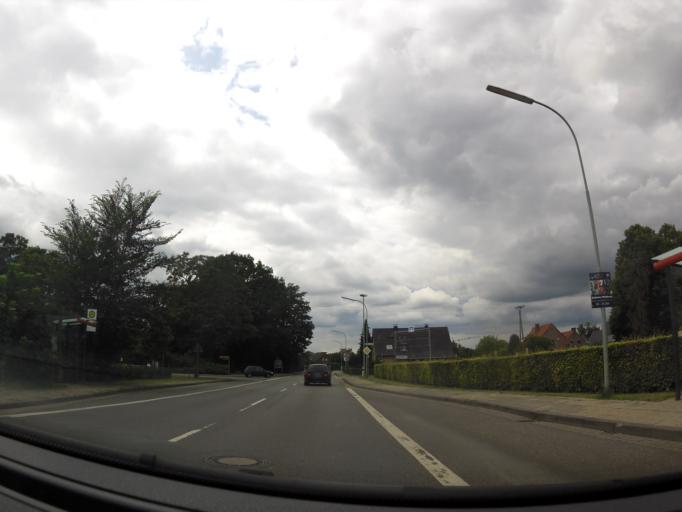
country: DE
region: North Rhine-Westphalia
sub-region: Regierungsbezirk Dusseldorf
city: Sonsbeck
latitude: 51.5680
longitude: 6.3711
